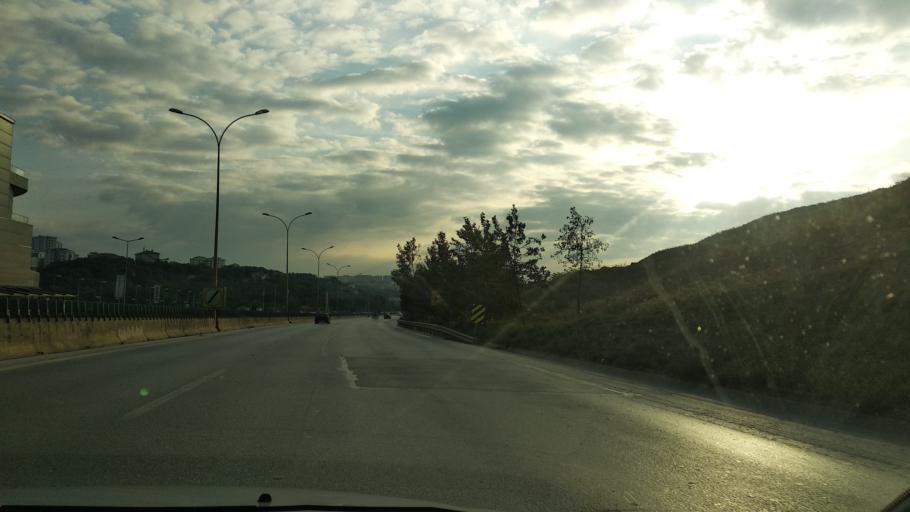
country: TR
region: Istanbul
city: Icmeler
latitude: 40.8874
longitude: 29.3240
